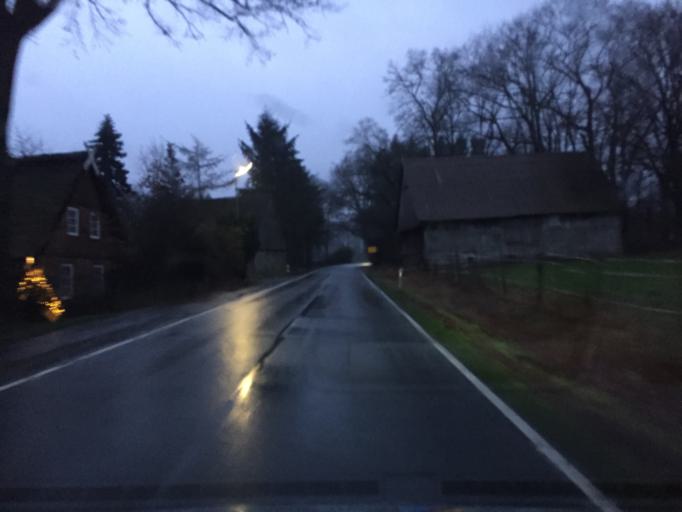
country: DE
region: Lower Saxony
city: Sudwalde
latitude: 52.8447
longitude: 8.8458
